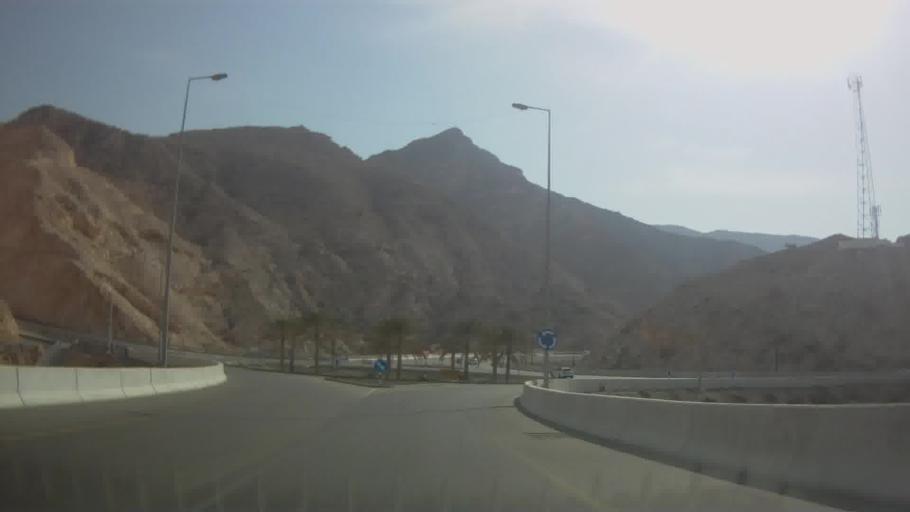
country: OM
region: Muhafazat Masqat
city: Muscat
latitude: 23.5416
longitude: 58.6476
